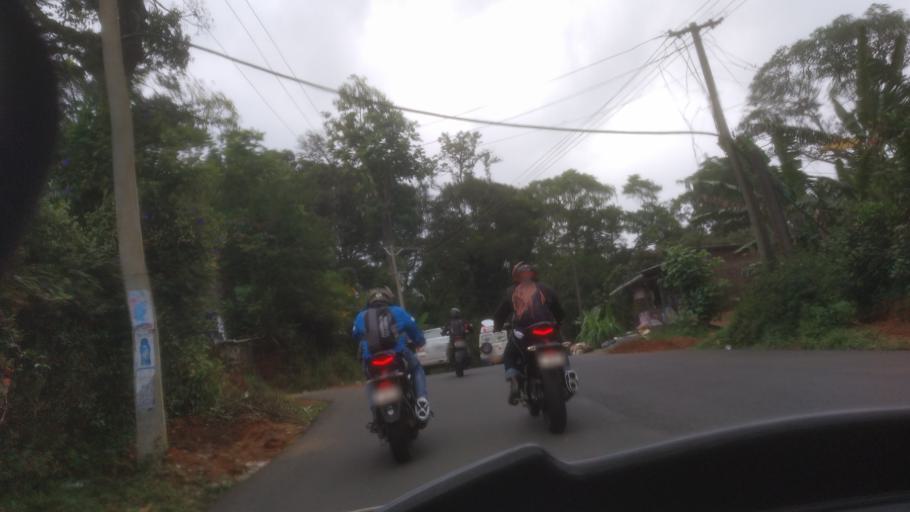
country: IN
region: Tamil Nadu
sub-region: Theni
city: Kombai
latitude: 9.8914
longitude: 77.1543
